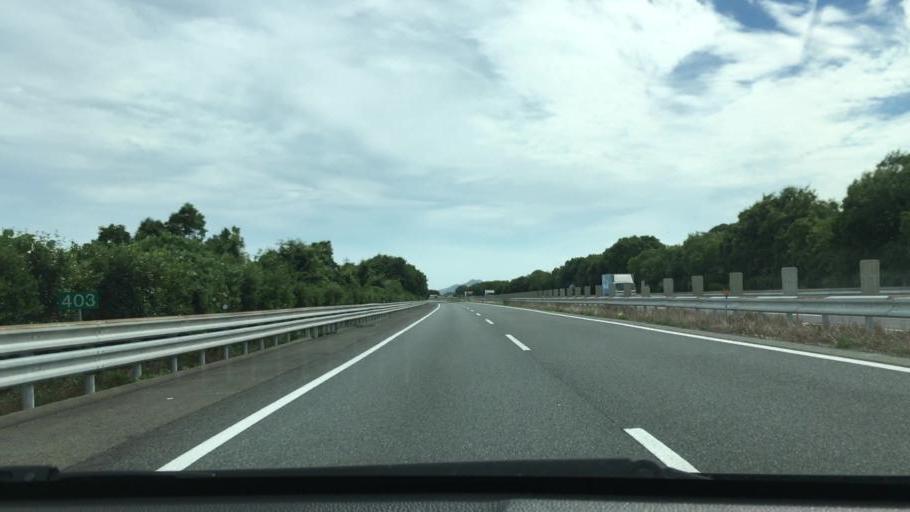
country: JP
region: Yamaguchi
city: Hofu
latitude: 34.0653
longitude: 131.5509
